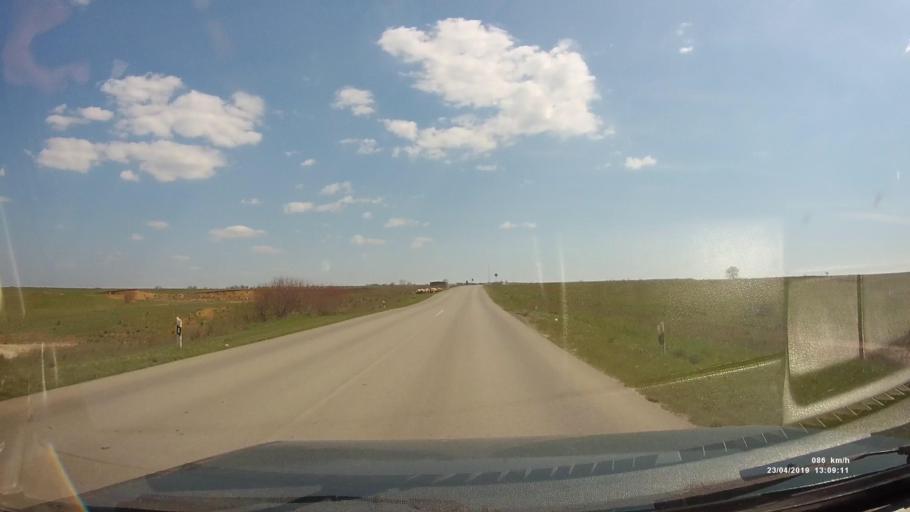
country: RU
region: Kalmykiya
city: Yashalta
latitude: 46.5772
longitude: 42.7860
